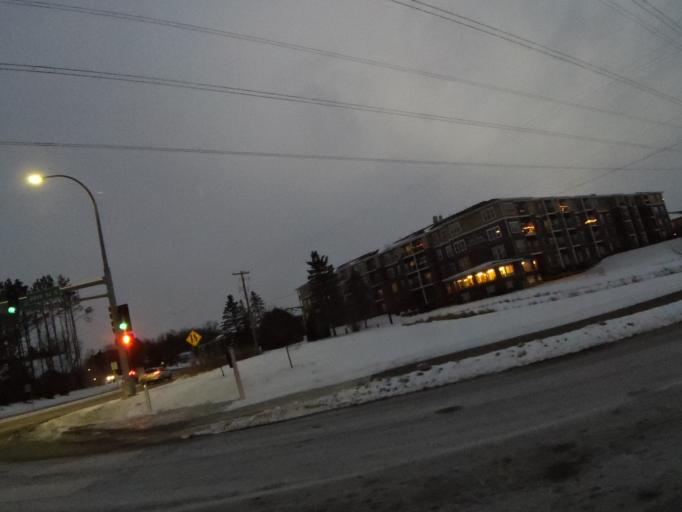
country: US
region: Minnesota
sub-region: Washington County
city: Stillwater
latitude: 45.0339
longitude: -92.8223
